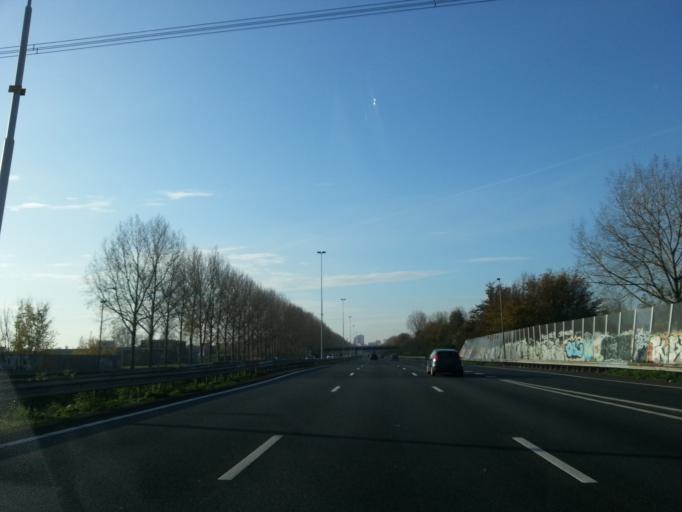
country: NL
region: South Holland
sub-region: Gemeente Capelle aan den IJssel
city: Capelle aan den IJssel
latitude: 51.9653
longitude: 4.5850
